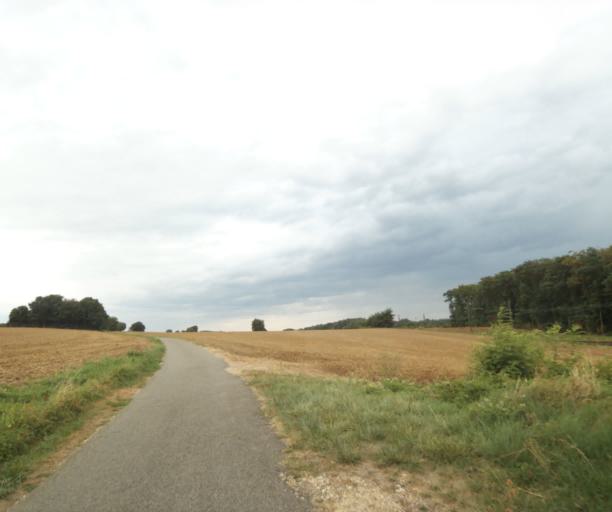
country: FR
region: Bourgogne
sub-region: Departement de Saone-et-Loire
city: Tournus
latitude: 46.5903
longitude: 4.9087
